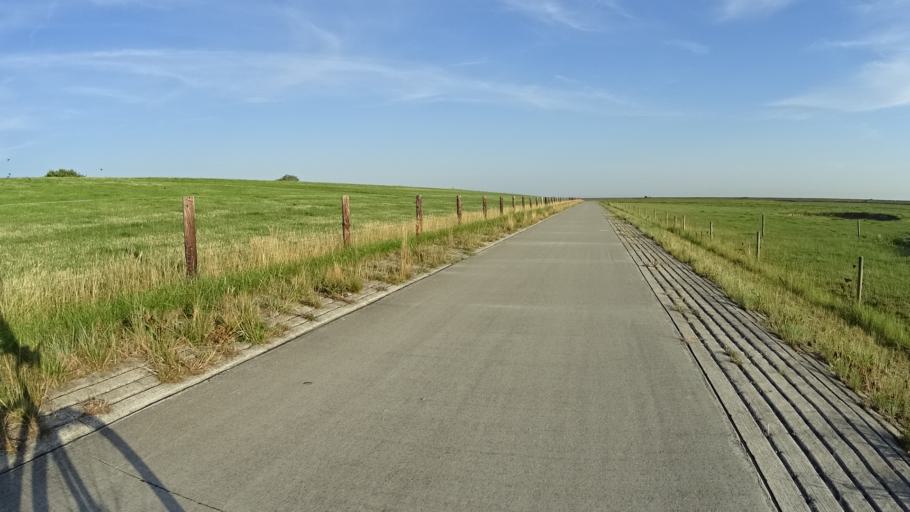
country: DE
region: Lower Saxony
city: Butjadingen
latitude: 53.6083
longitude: 8.3230
